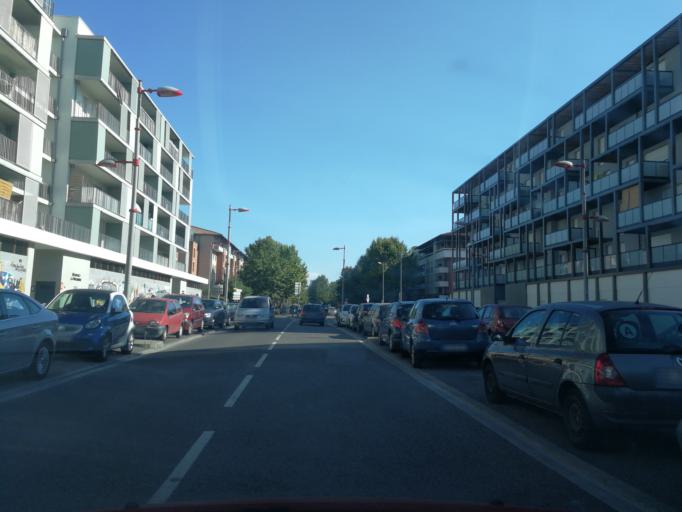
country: FR
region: Midi-Pyrenees
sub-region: Departement de la Haute-Garonne
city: Toulouse
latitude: 43.6395
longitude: 1.4526
